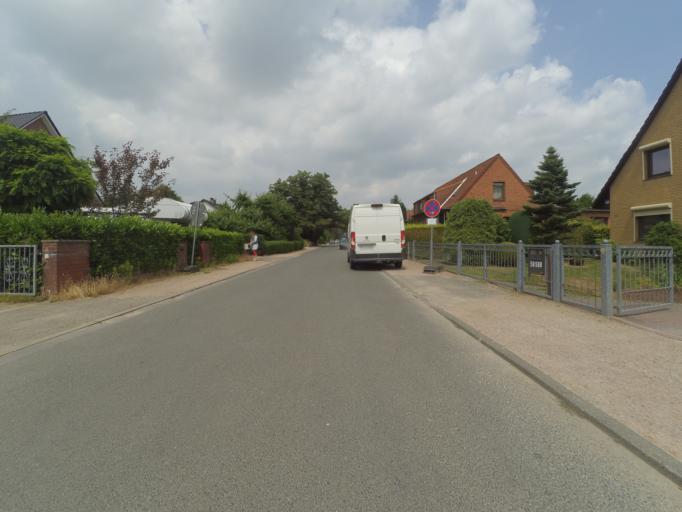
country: DE
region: Hamburg
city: Sasel
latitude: 53.6460
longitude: 10.1165
